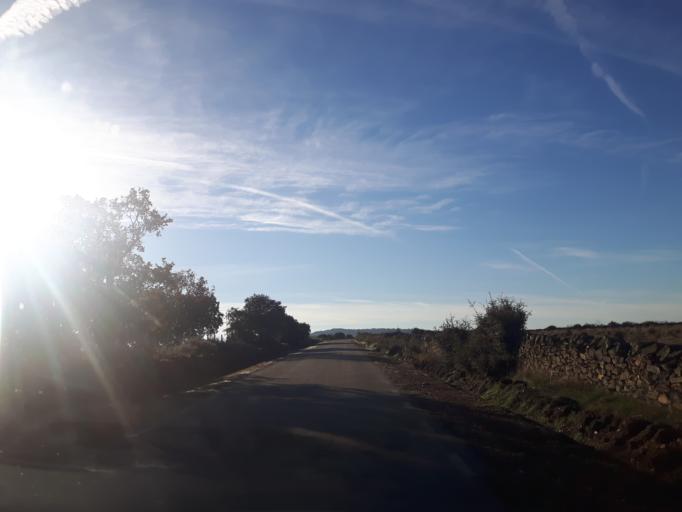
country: ES
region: Castille and Leon
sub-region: Provincia de Salamanca
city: Olmedo de Camaces
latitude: 40.9225
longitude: -6.6171
